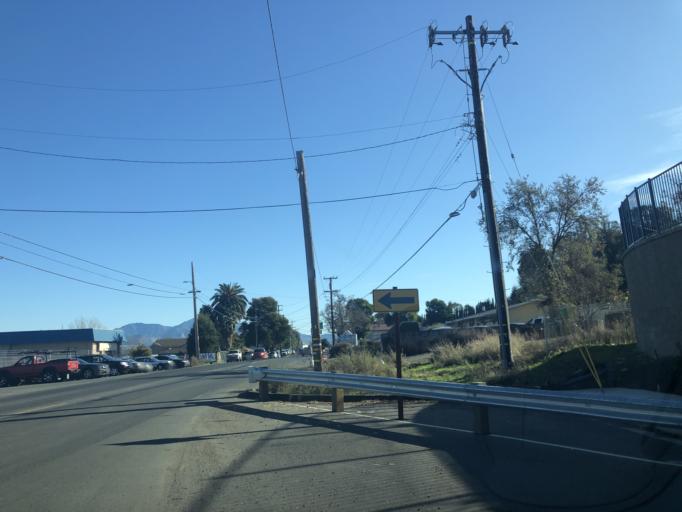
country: US
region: California
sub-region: Contra Costa County
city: Pacheco
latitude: 37.9974
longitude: -122.0772
